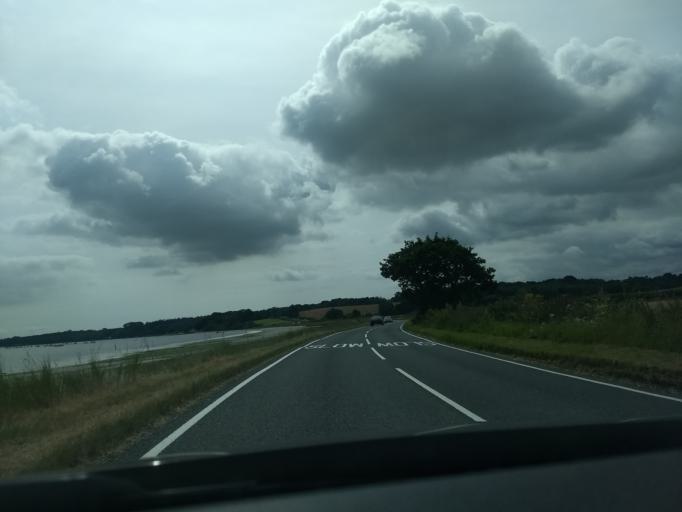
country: GB
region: England
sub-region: Suffolk
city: Ipswich
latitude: 52.0233
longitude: 1.1634
